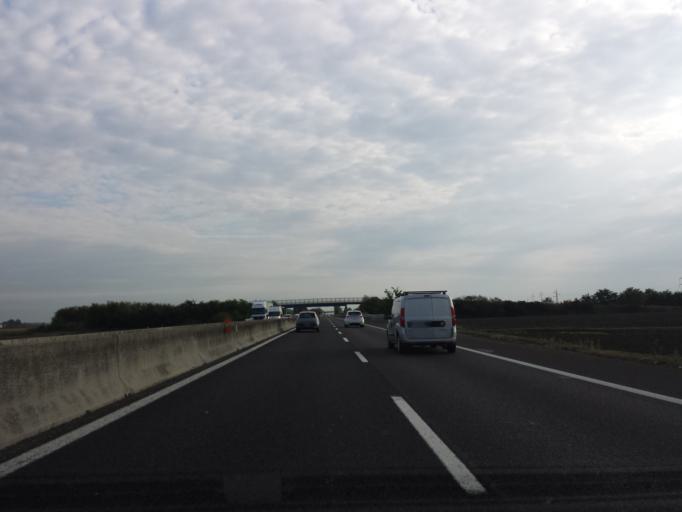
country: IT
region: Veneto
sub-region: Provincia di Padova
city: Pozzonovo
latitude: 45.1943
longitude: 11.7753
